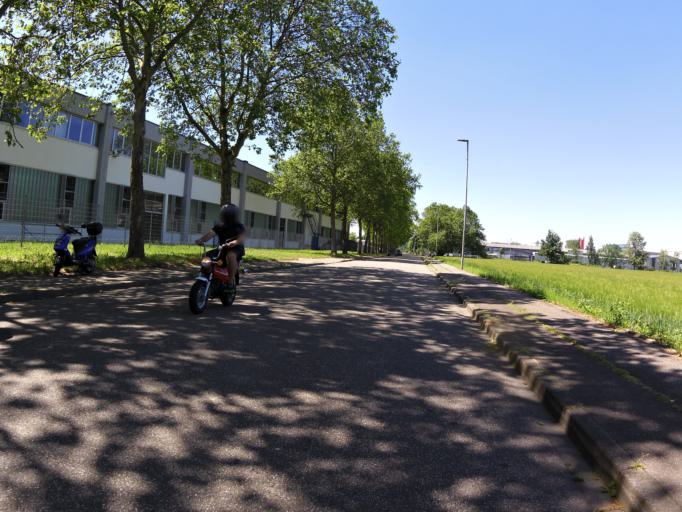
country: DE
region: Baden-Wuerttemberg
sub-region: Freiburg Region
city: Lahr
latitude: 48.3389
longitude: 7.8261
